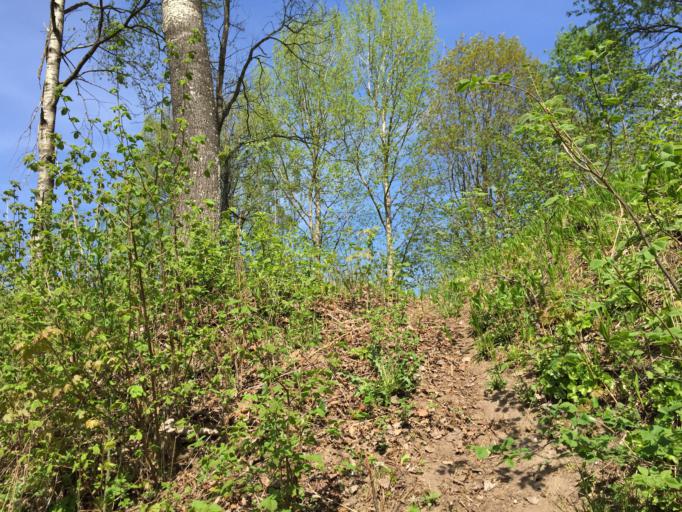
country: LV
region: Limbazu Rajons
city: Limbazi
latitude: 57.3543
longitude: 24.6560
